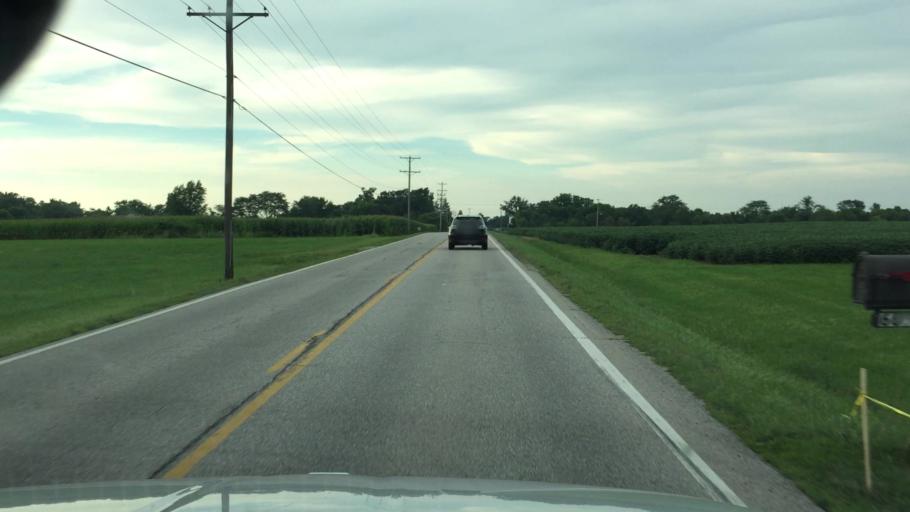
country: US
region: Ohio
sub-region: Madison County
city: Plain City
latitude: 40.0384
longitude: -83.2632
